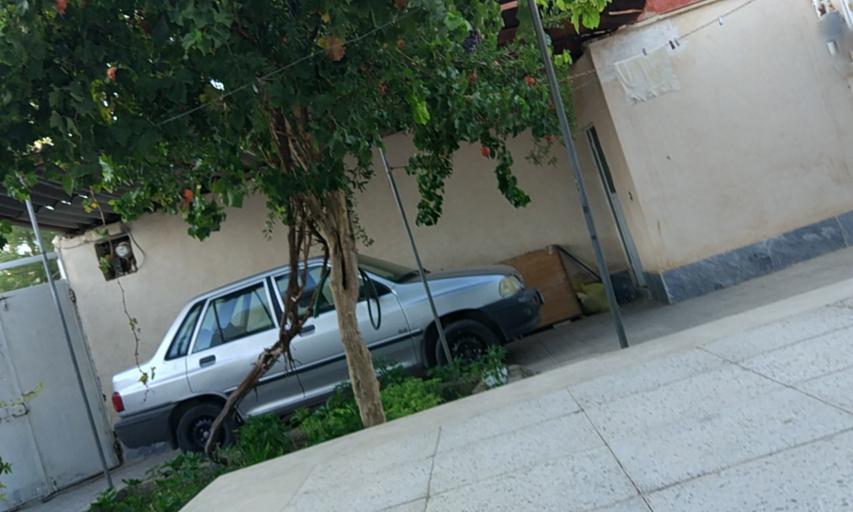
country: IR
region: Khorasan-e Jonubi
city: Birjand
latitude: 32.8501
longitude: 59.2117
